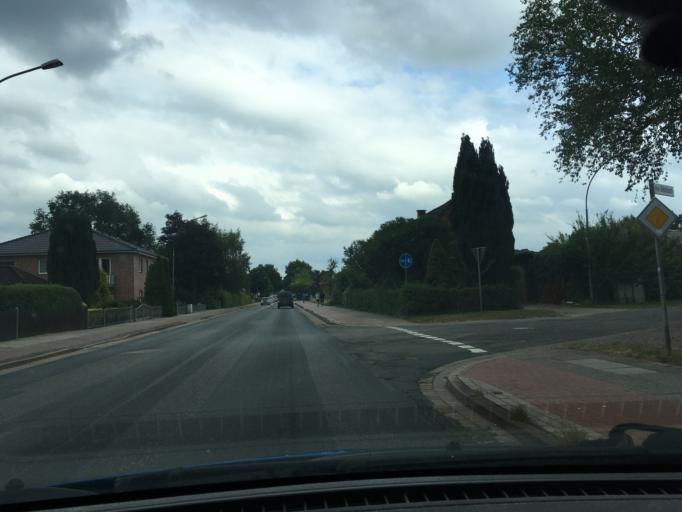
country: DE
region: Lower Saxony
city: Tostedt
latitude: 53.2718
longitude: 9.7217
